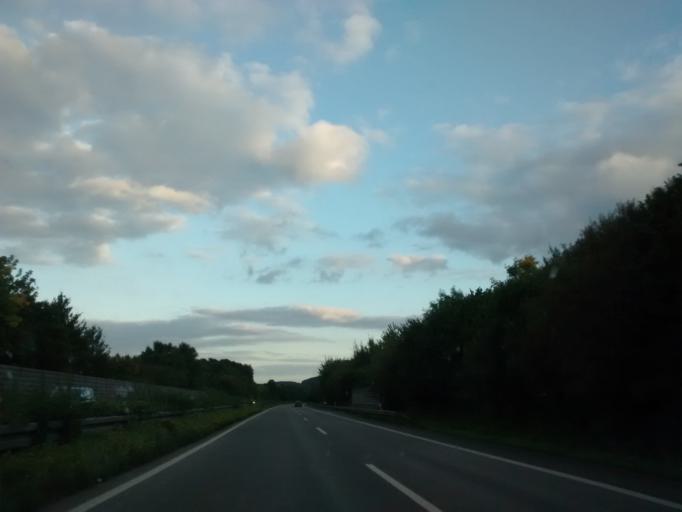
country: DE
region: Lower Saxony
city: Bissendorf
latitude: 52.2131
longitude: 8.1212
